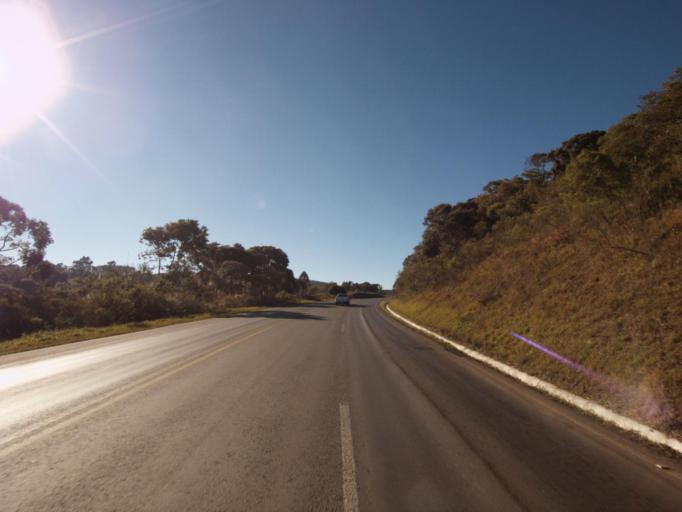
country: BR
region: Santa Catarina
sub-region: Concordia
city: Concordia
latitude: -26.8885
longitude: -51.9907
